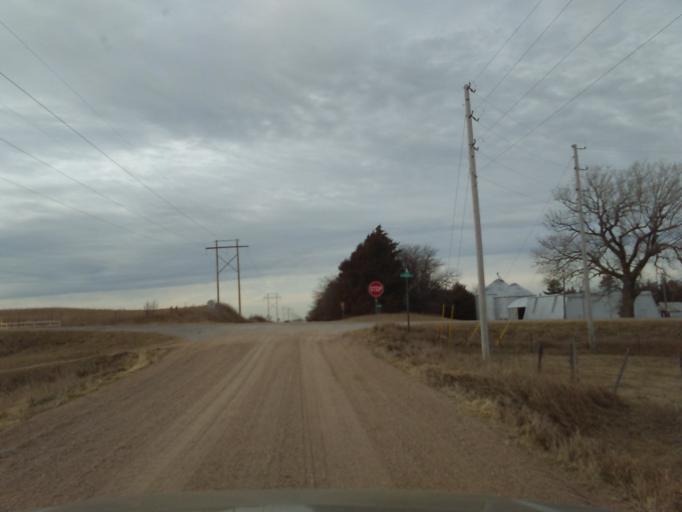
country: US
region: Nebraska
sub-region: Buffalo County
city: Shelton
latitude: 40.6548
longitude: -98.7237
